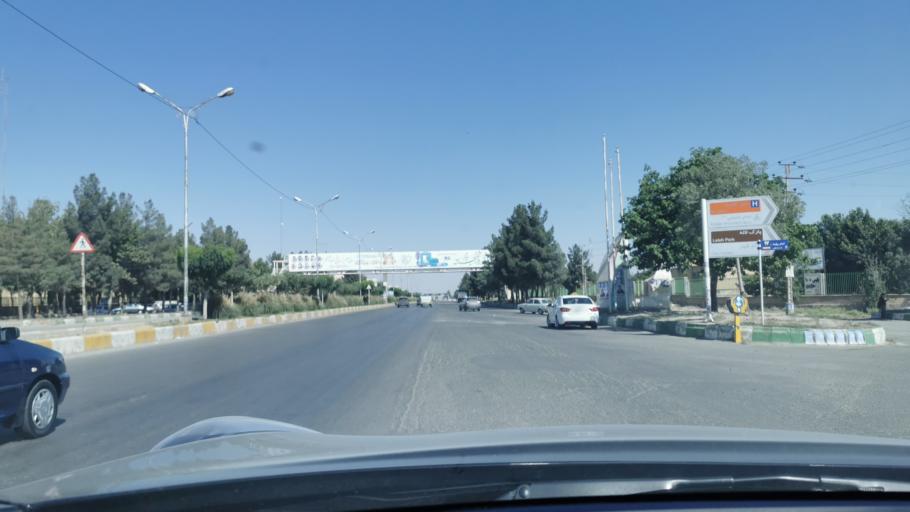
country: IR
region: Razavi Khorasan
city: Chenaran
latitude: 36.6374
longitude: 59.1244
